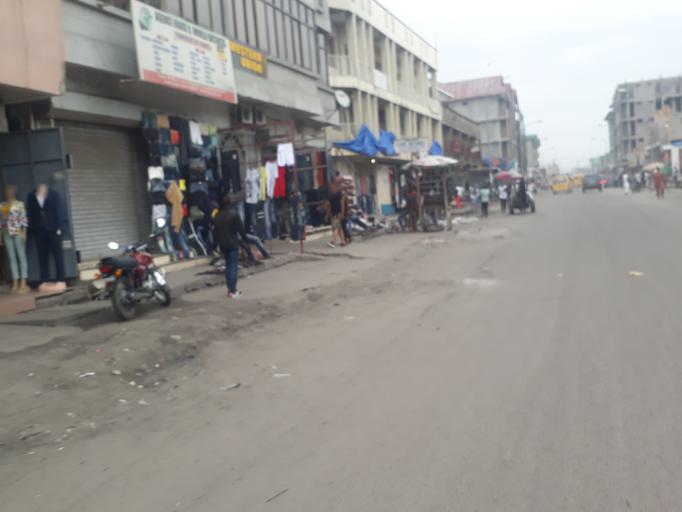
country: CD
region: Kinshasa
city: Kinshasa
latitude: -4.3138
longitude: 15.3096
